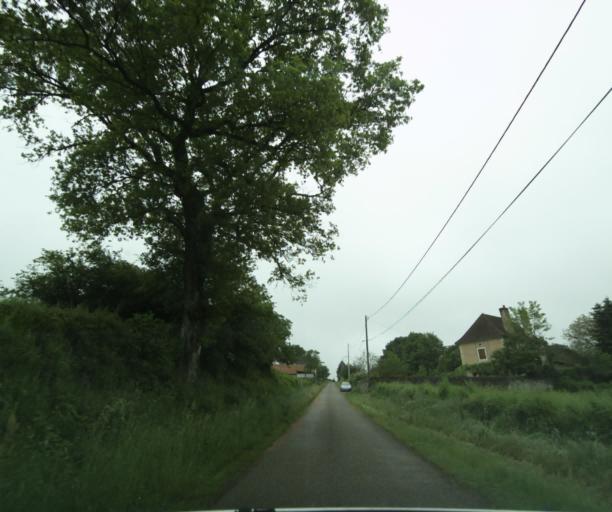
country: FR
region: Bourgogne
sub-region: Departement de Saone-et-Loire
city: Charolles
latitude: 46.4334
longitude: 4.4137
